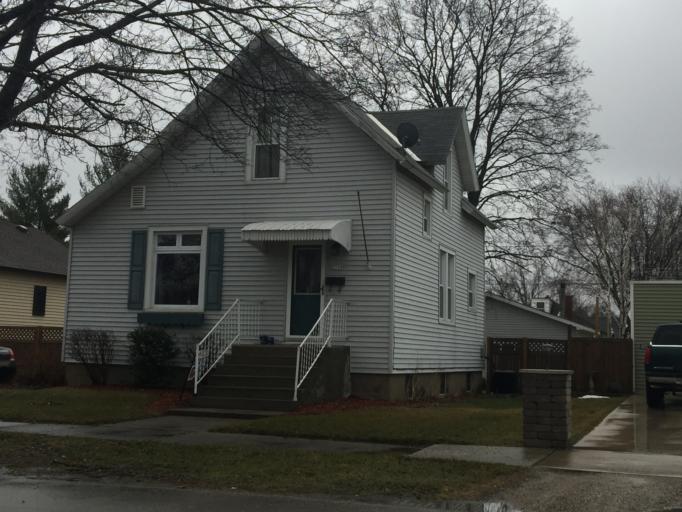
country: US
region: Wisconsin
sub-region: Marinette County
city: Marinette
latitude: 45.1135
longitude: -87.6297
